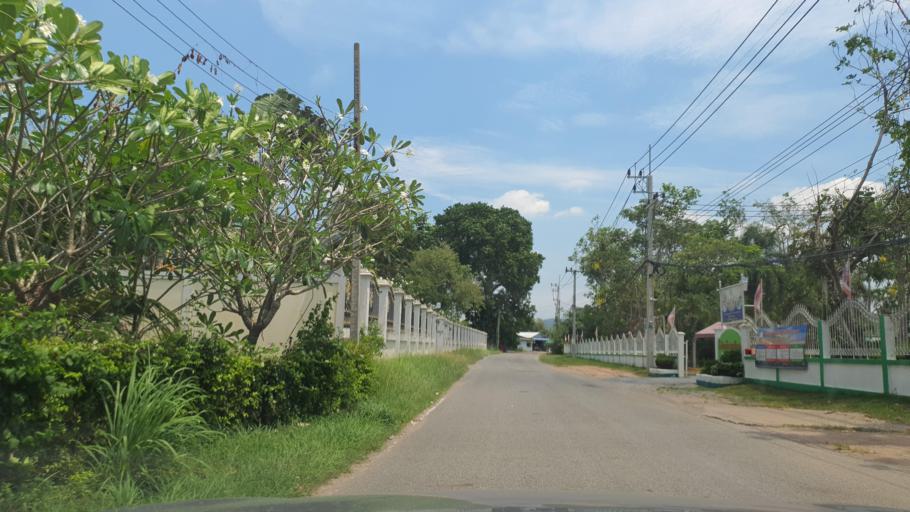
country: TH
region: Rayong
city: Ban Chang
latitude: 12.8064
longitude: 100.9480
